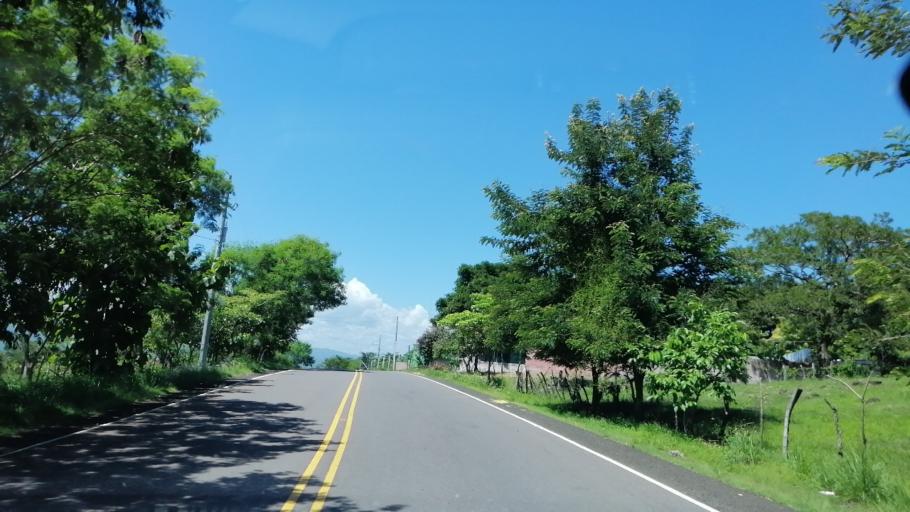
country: SV
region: Morazan
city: Cacaopera
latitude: 13.8092
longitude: -88.1553
